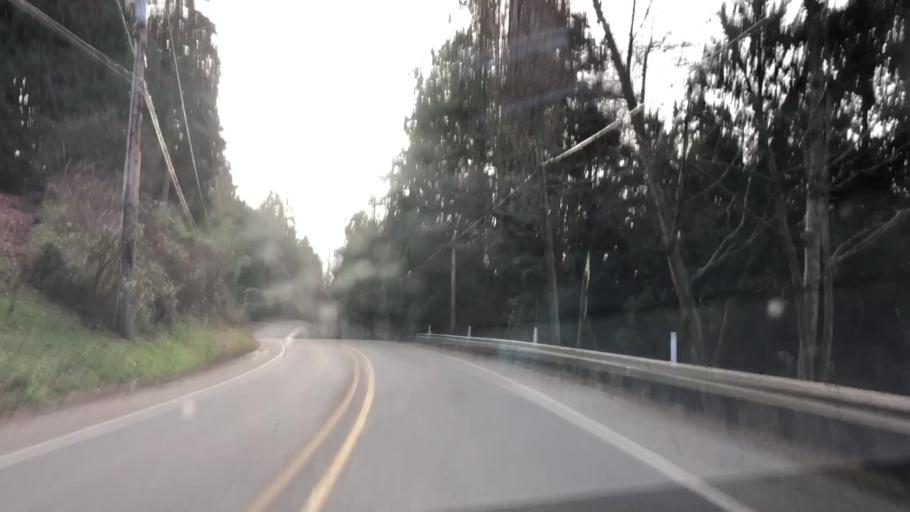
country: US
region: Washington
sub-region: Kitsap County
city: Suquamish
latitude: 47.7573
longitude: -122.5506
